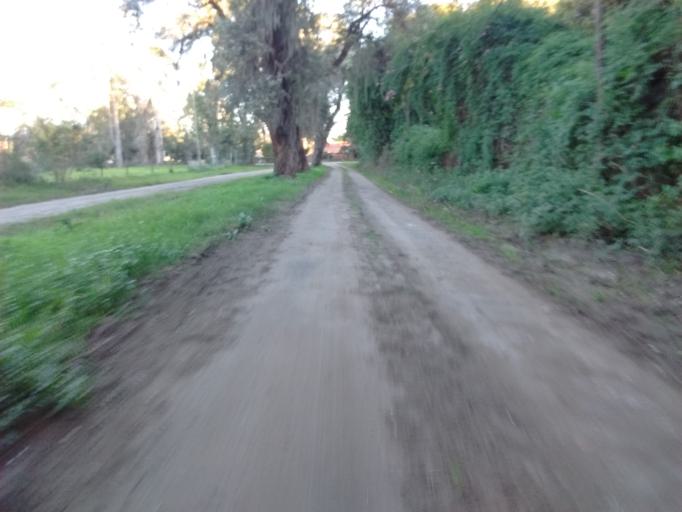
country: AR
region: Santa Fe
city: Funes
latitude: -32.9168
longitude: -60.8328
